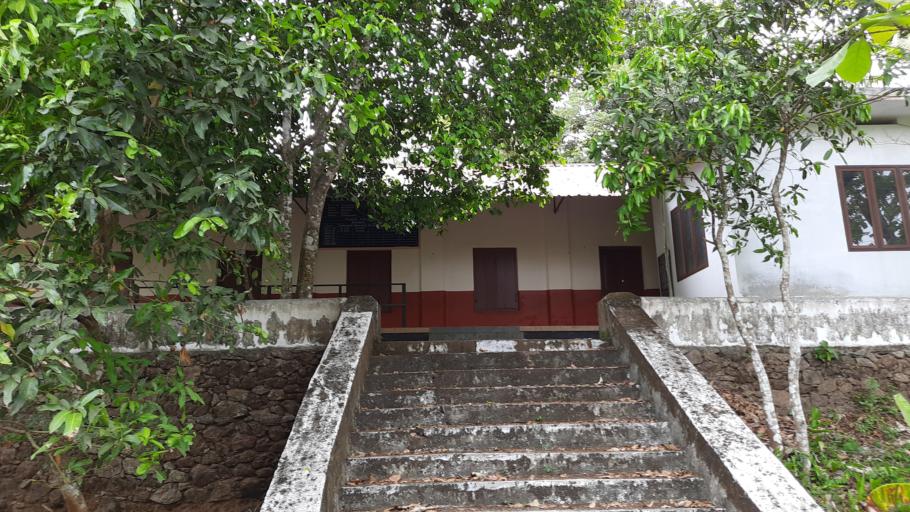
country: IN
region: Kerala
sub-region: Kottayam
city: Lalam
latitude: 9.8377
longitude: 76.7238
